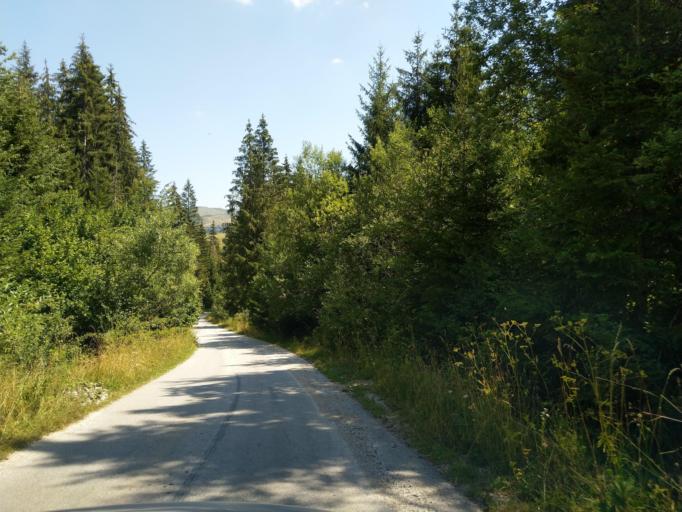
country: RS
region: Central Serbia
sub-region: Zlatiborski Okrug
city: Nova Varos
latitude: 43.4719
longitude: 19.9627
